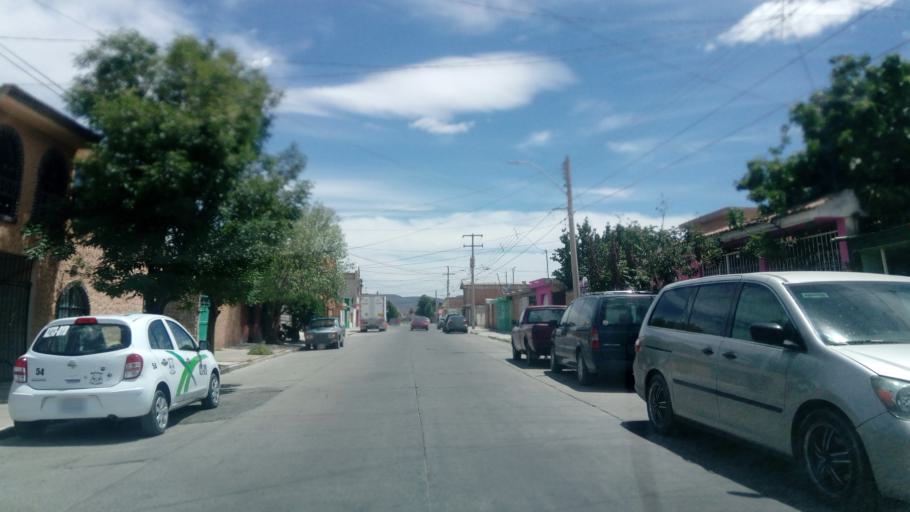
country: MX
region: Durango
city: Victoria de Durango
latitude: 23.9953
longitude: -104.6764
